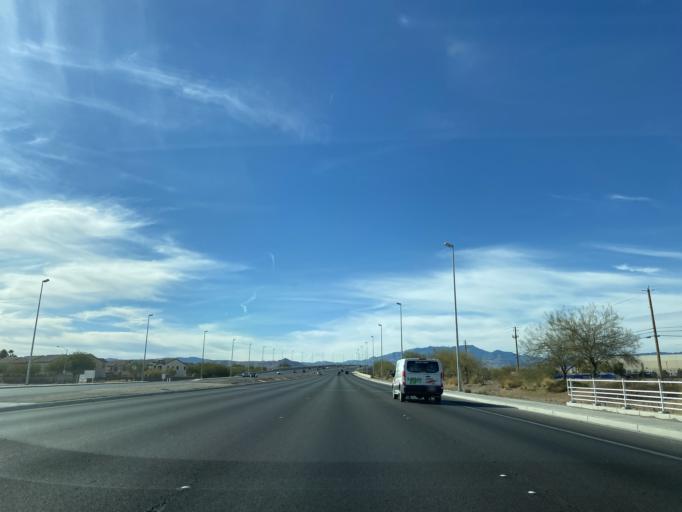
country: US
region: Nevada
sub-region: Clark County
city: Enterprise
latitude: 36.0283
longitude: -115.2178
